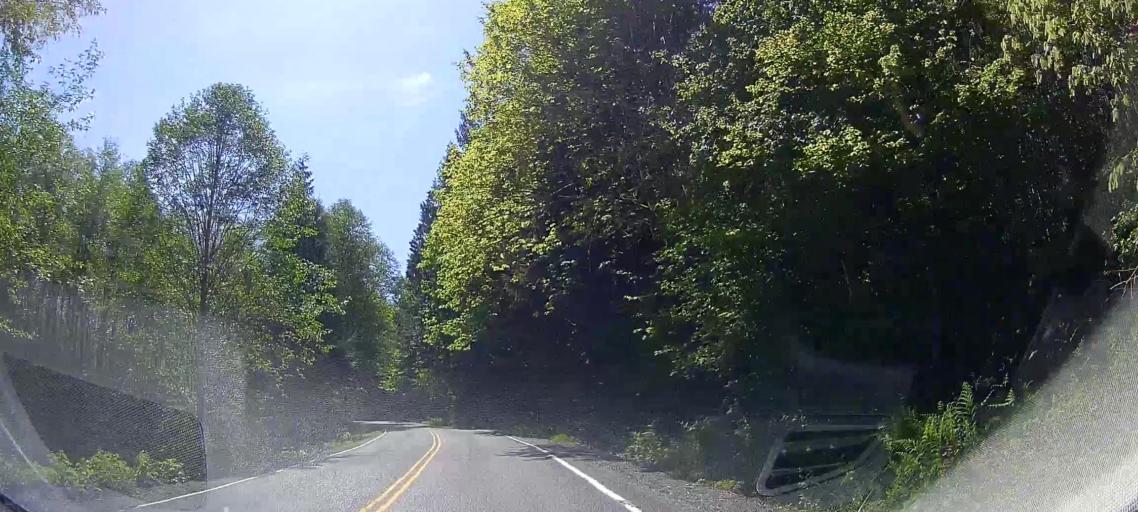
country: US
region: Washington
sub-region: Snohomish County
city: Darrington
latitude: 48.4675
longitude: -121.6175
